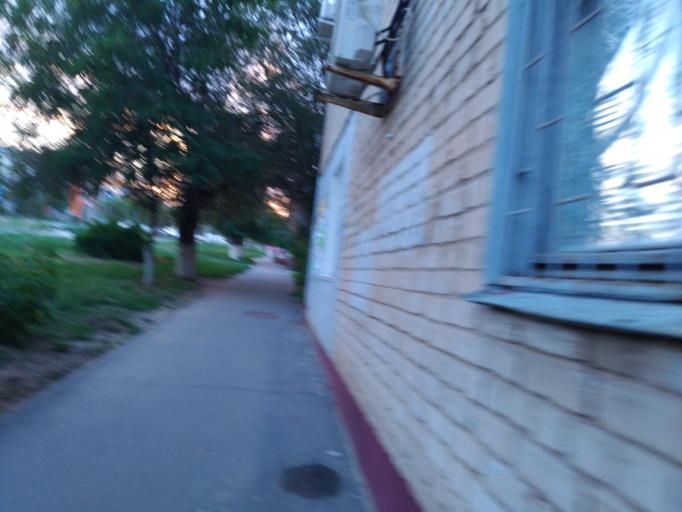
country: RU
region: Volgograd
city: Volgograd
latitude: 48.6730
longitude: 44.4469
